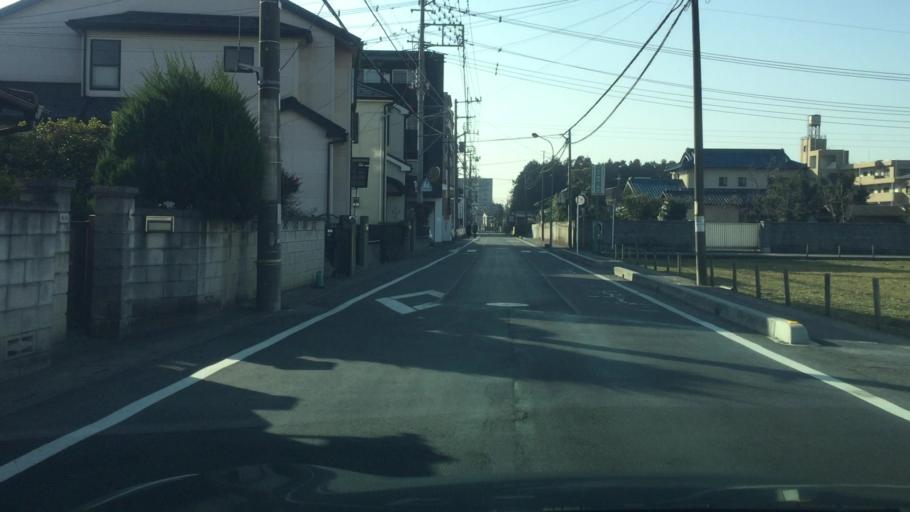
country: JP
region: Saitama
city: Ageoshimo
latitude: 35.9310
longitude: 139.6134
